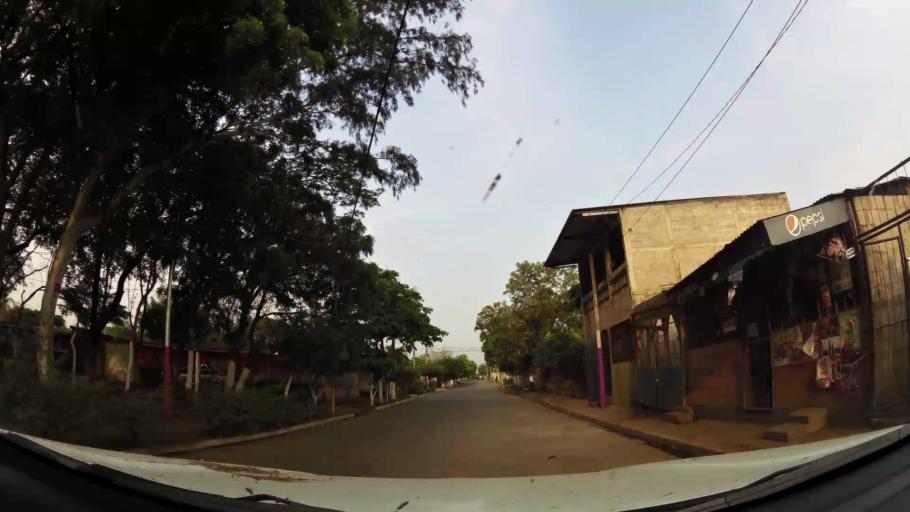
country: NI
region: Masaya
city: Masaya
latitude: 11.9831
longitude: -86.0845
